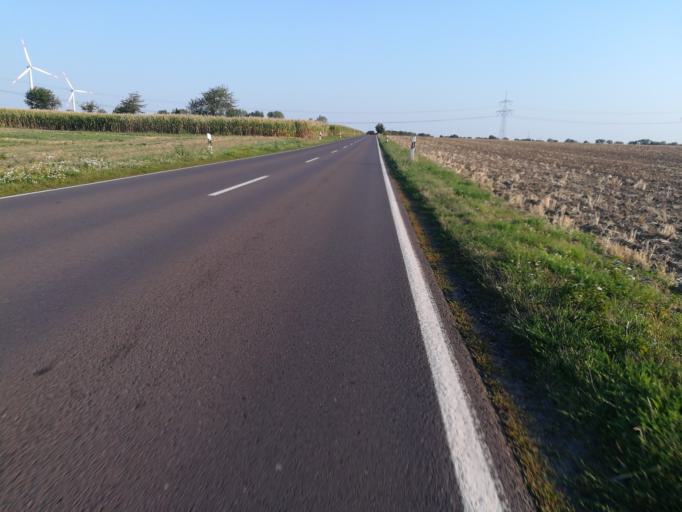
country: DE
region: Saxony-Anhalt
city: Irxleben
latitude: 52.1695
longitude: 11.4765
